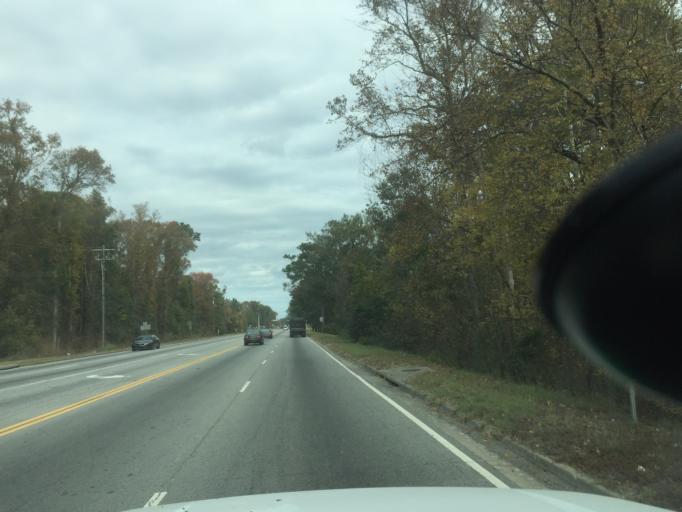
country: US
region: Georgia
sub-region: Chatham County
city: Garden City
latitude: 32.0931
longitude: -81.1966
